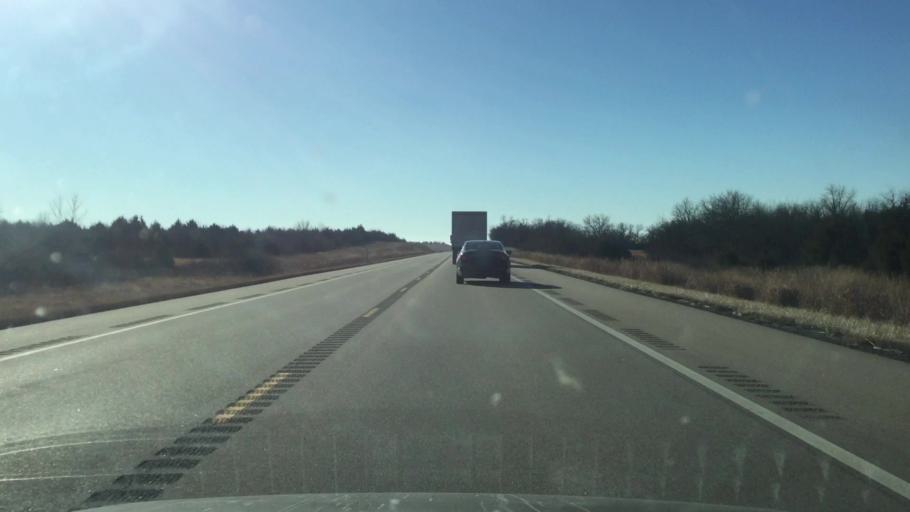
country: US
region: Kansas
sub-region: Allen County
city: Iola
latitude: 38.0367
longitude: -95.3806
